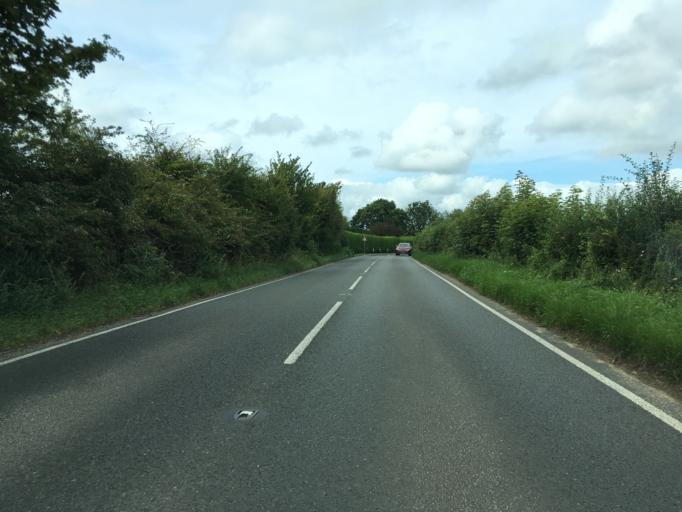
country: GB
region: England
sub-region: Kent
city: Royal Tunbridge Wells
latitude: 51.1261
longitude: 0.1936
